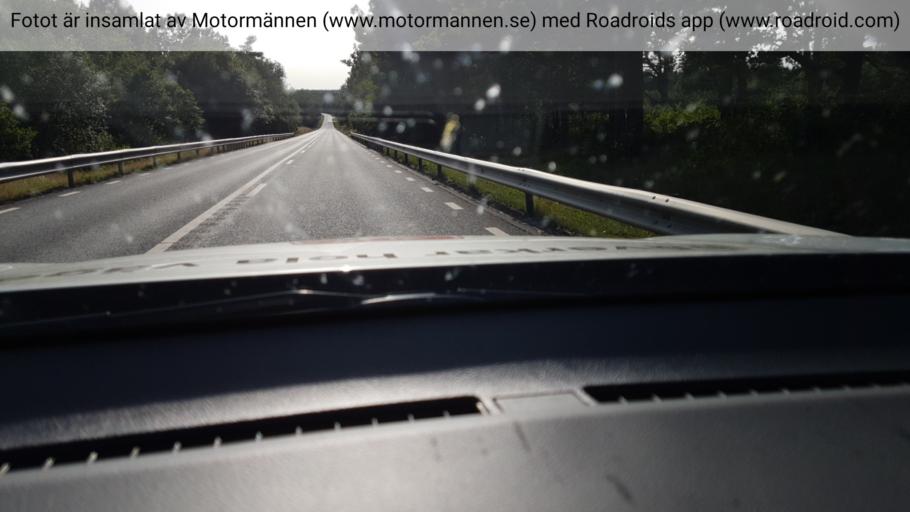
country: SE
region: Joenkoeping
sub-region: Varnamo Kommun
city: Varnamo
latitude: 57.2266
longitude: 14.1443
